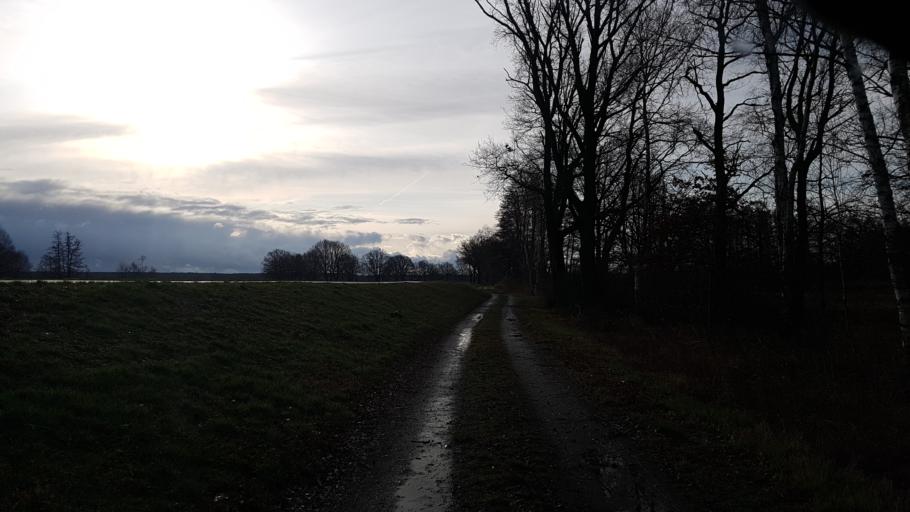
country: DE
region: Brandenburg
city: Herzberg
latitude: 51.6676
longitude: 13.2615
